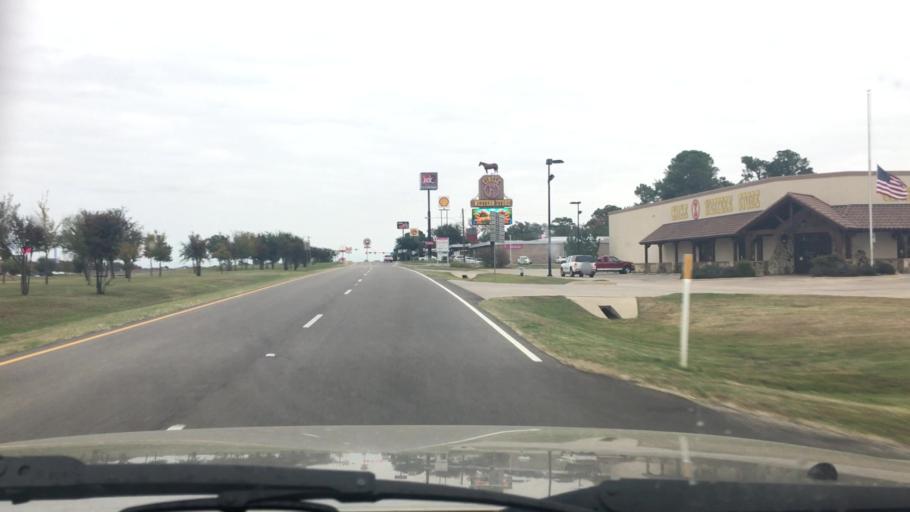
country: US
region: Texas
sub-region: Hopkins County
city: Sulphur Springs
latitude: 33.1159
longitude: -95.6003
